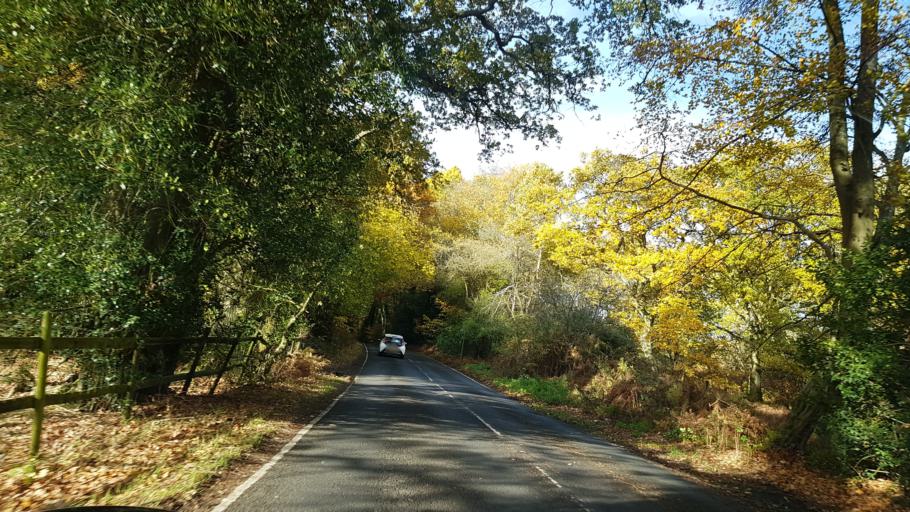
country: GB
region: England
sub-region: Surrey
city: Seale
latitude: 51.1993
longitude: -0.7453
